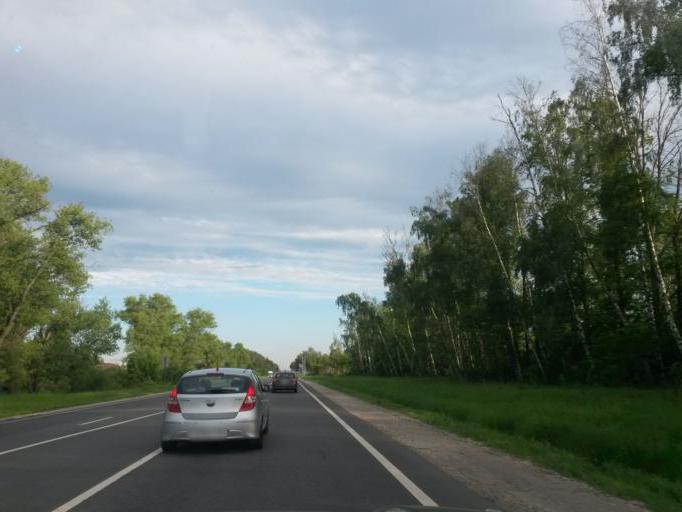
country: RU
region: Moskovskaya
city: Belyye Stolby
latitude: 55.3282
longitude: 37.8055
